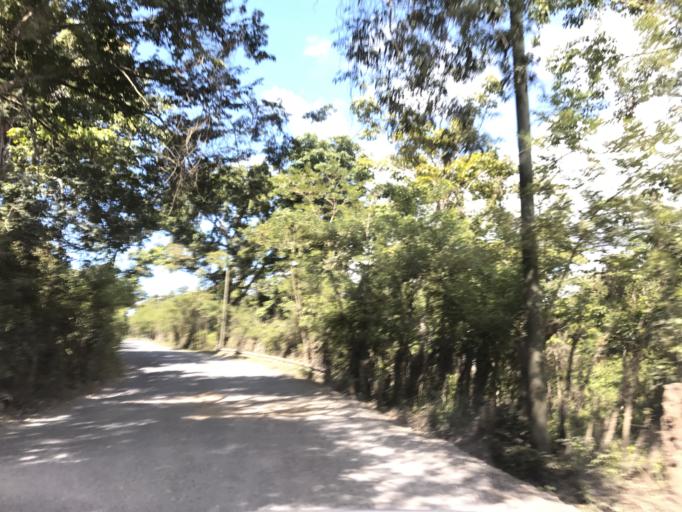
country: GT
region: Izabal
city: Morales
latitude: 15.6427
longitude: -89.0297
